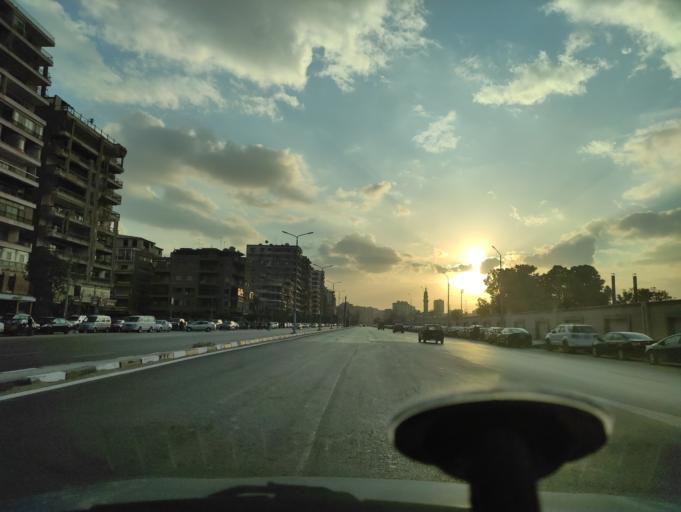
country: EG
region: Muhafazat al Qalyubiyah
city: Al Khankah
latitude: 30.1184
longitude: 31.3489
